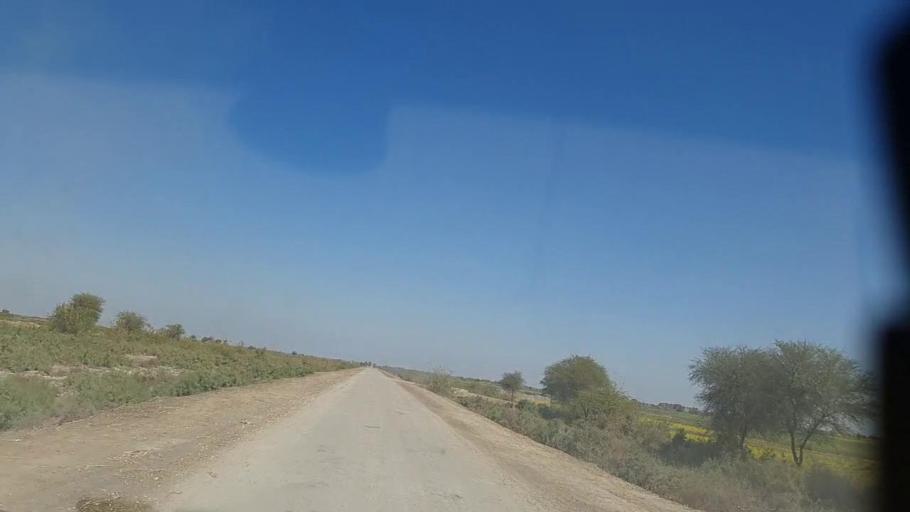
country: PK
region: Sindh
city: Mirwah Gorchani
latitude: 25.2334
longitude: 69.0208
